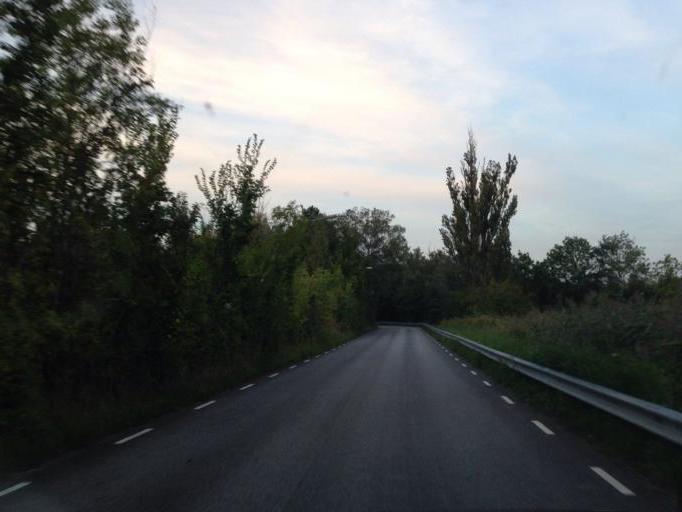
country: SE
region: Skane
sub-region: Lomma Kommun
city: Lomma
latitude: 55.6834
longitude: 13.0732
